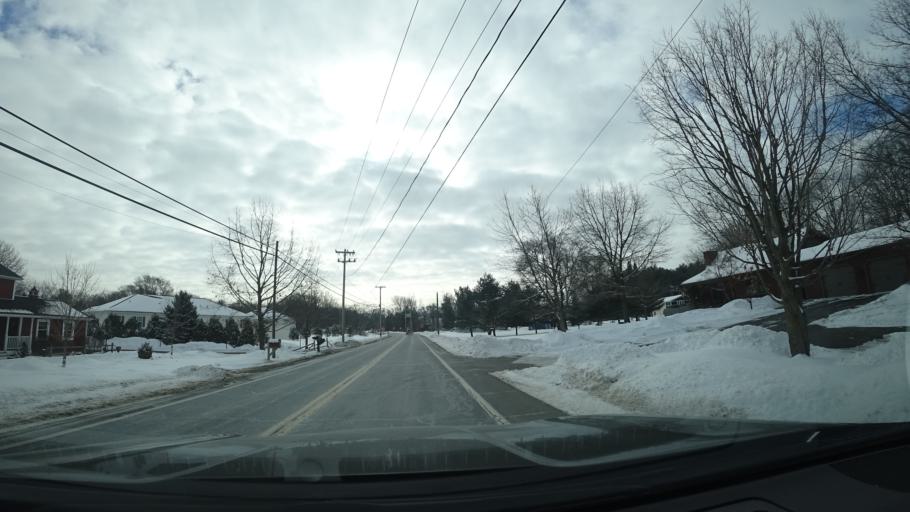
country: US
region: New York
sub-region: Saratoga County
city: South Glens Falls
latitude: 43.2856
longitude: -73.6225
